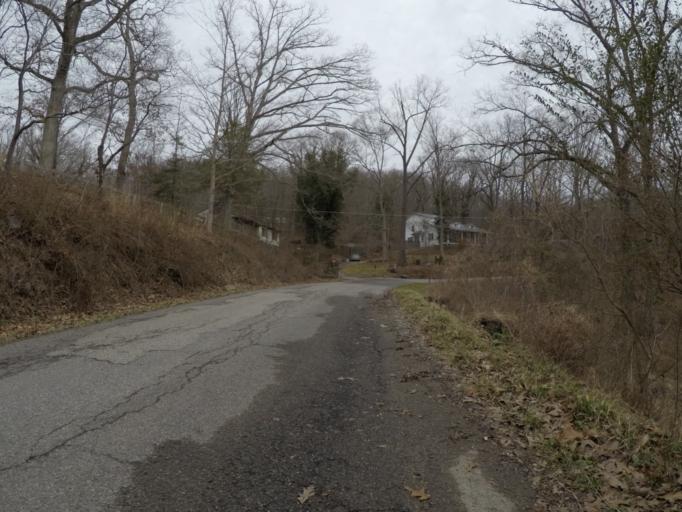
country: US
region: Ohio
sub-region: Lawrence County
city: Burlington
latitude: 38.3868
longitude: -82.5087
